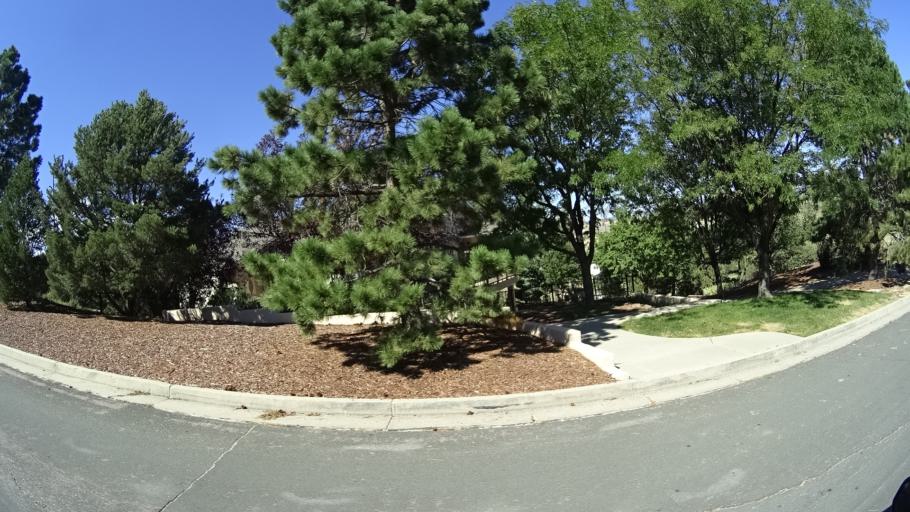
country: US
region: Colorado
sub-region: El Paso County
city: Colorado Springs
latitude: 38.8621
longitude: -104.8445
